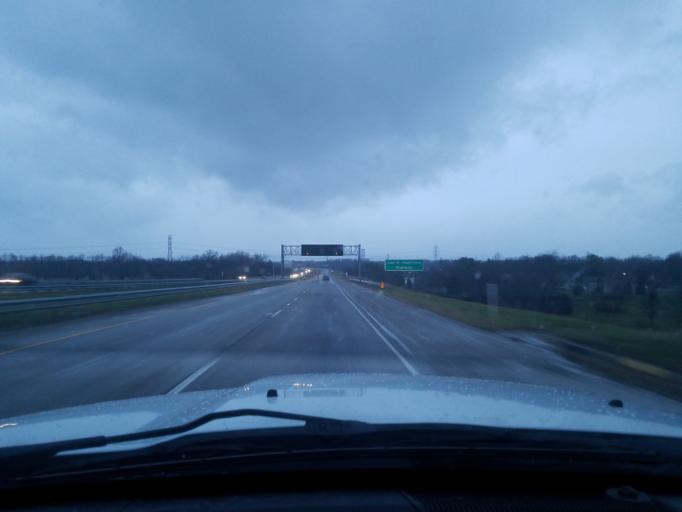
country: US
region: Indiana
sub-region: Clark County
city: Oak Park
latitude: 38.3454
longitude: -85.7190
